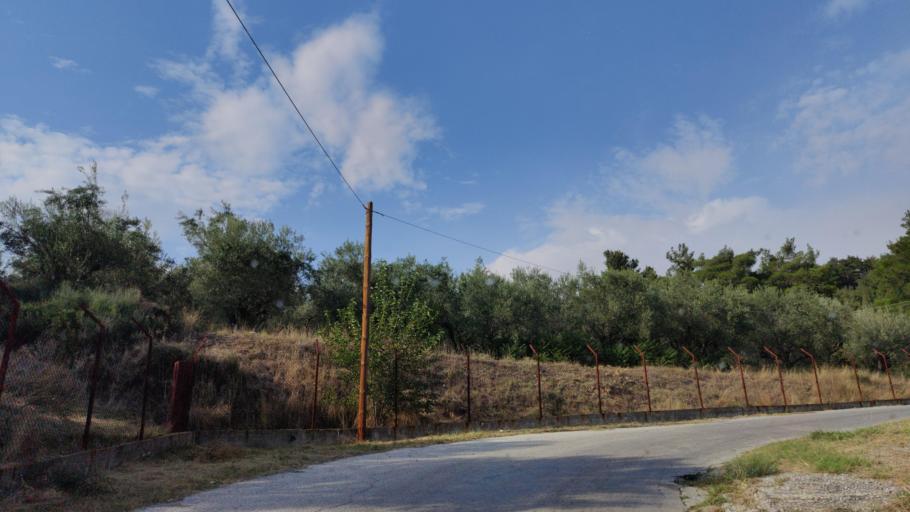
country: GR
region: Central Macedonia
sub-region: Nomos Serron
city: Sidirokastro
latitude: 41.2350
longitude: 23.4000
